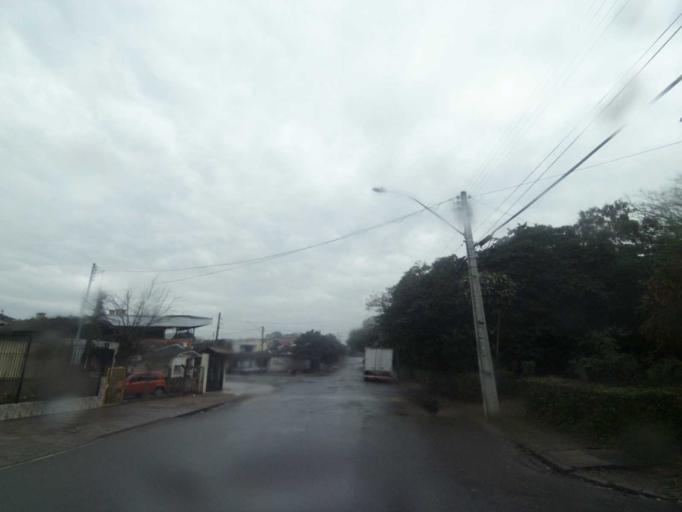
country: BR
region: Rio Grande do Sul
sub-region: Sao Leopoldo
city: Sao Leopoldo
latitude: -29.7891
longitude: -51.1653
